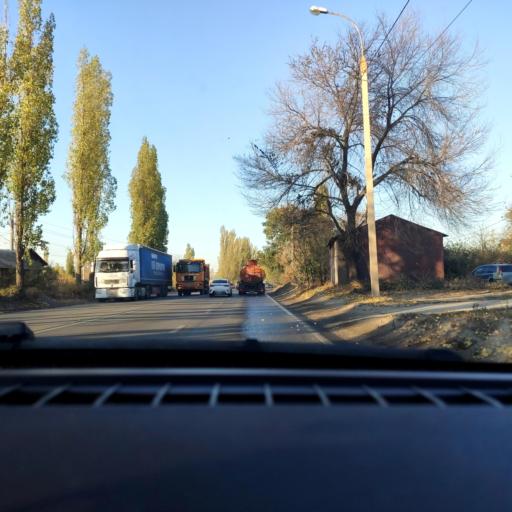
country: RU
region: Voronezj
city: Maslovka
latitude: 51.6172
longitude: 39.2585
